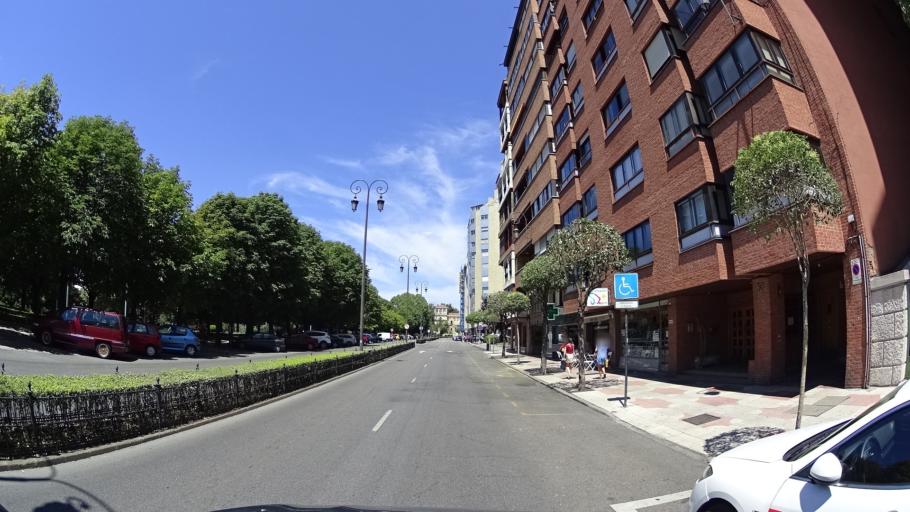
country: ES
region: Castille and Leon
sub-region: Provincia de Leon
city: Leon
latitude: 42.5993
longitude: -5.5804
